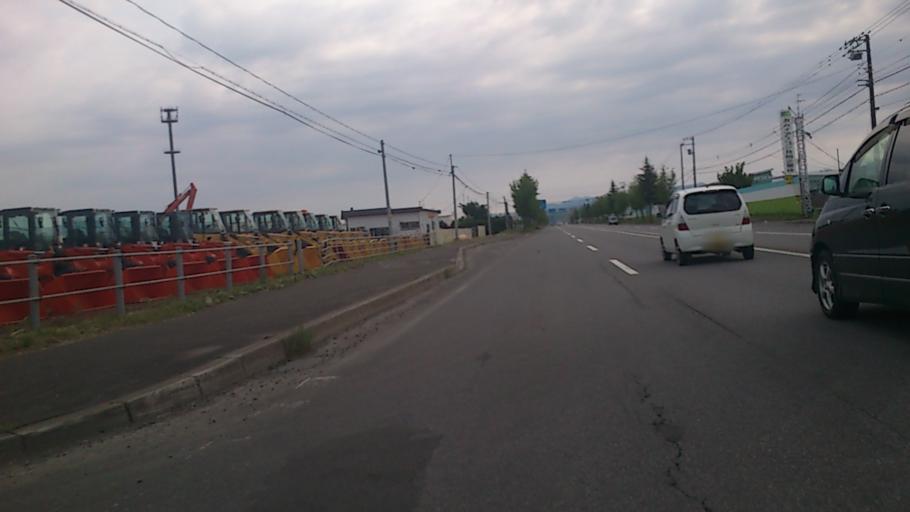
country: JP
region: Hokkaido
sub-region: Asahikawa-shi
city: Asahikawa
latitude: 43.8417
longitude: 142.4838
